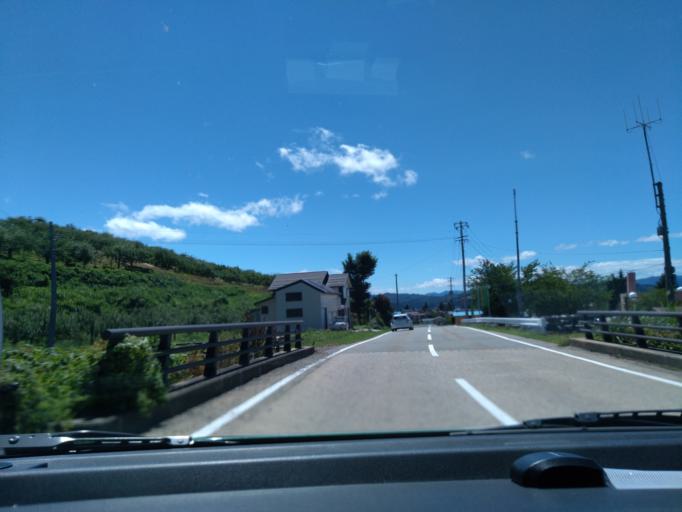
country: JP
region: Akita
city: Yokotemachi
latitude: 39.2336
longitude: 140.5657
